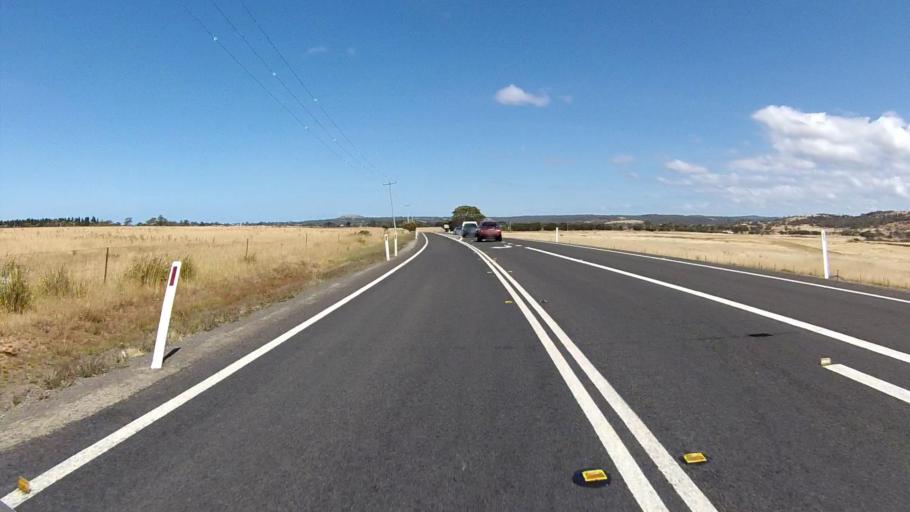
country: AU
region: Tasmania
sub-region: Break O'Day
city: St Helens
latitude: -42.0983
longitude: 148.0631
